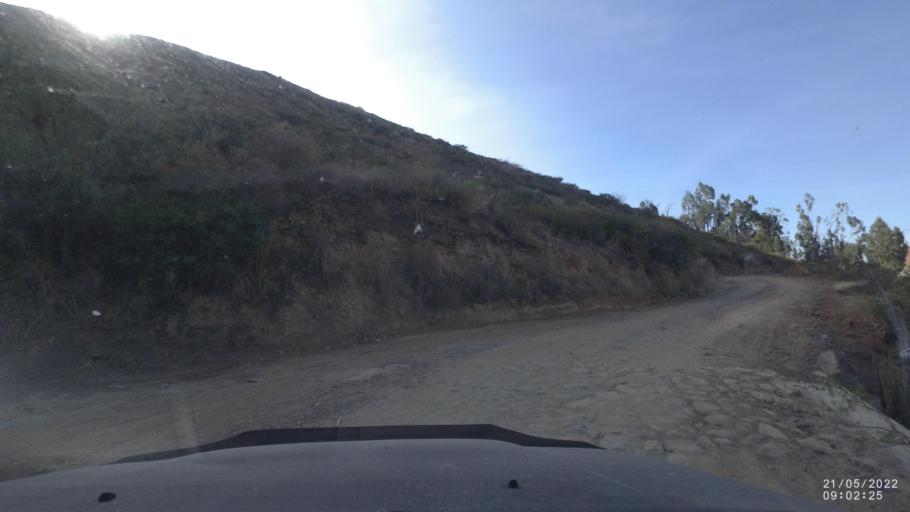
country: BO
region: Cochabamba
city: Cochabamba
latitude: -17.3762
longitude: -66.0305
